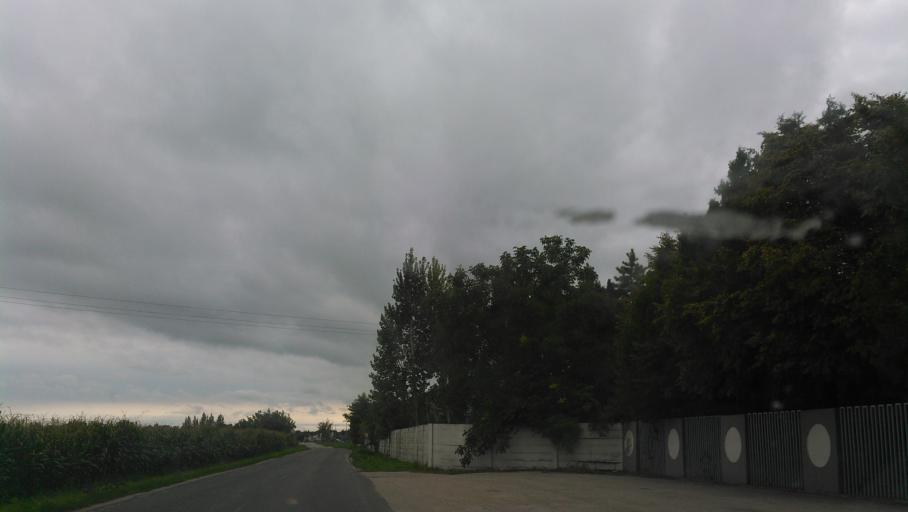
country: SK
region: Trnavsky
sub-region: Okres Dunajska Streda
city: Velky Meder
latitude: 47.9327
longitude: 17.7254
